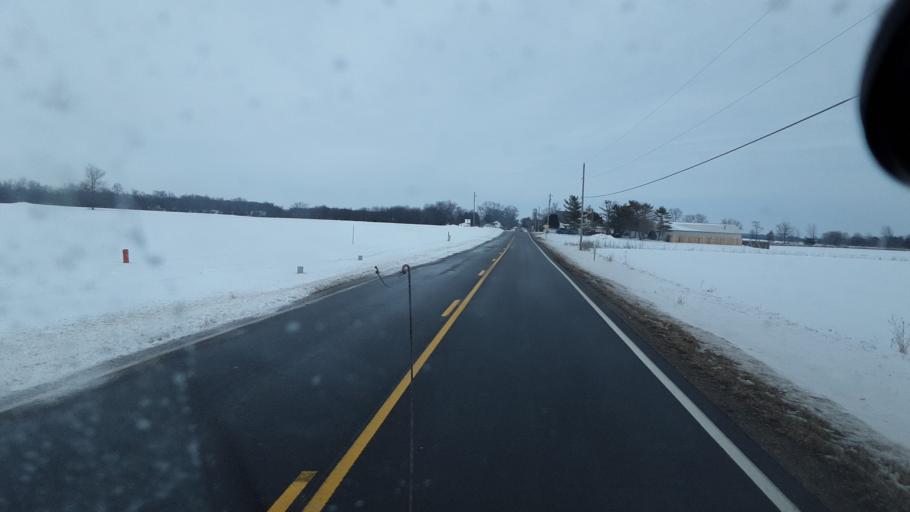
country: US
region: Ohio
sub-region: Union County
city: New California
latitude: 40.2118
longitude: -83.2546
